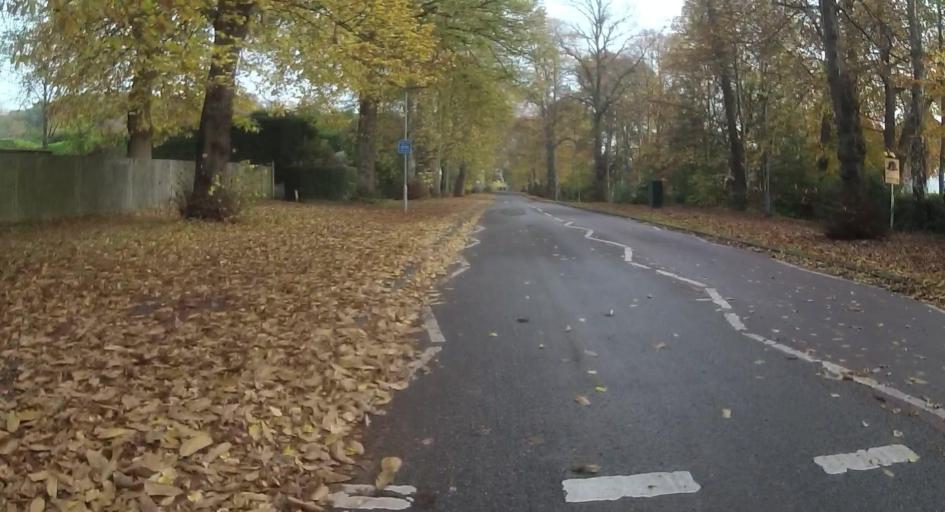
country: GB
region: England
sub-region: Bracknell Forest
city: Crowthorne
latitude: 51.3659
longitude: -0.7902
